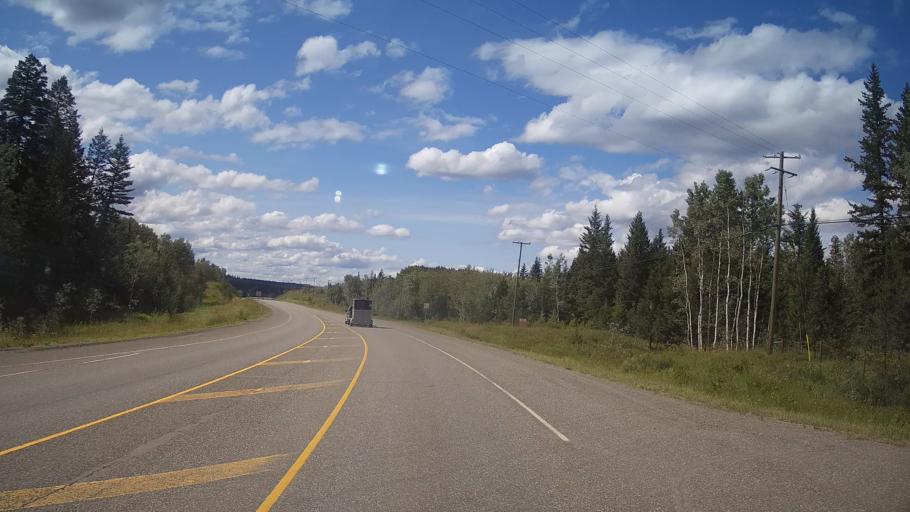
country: CA
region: British Columbia
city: Williams Lake
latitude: 51.8605
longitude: -121.6423
